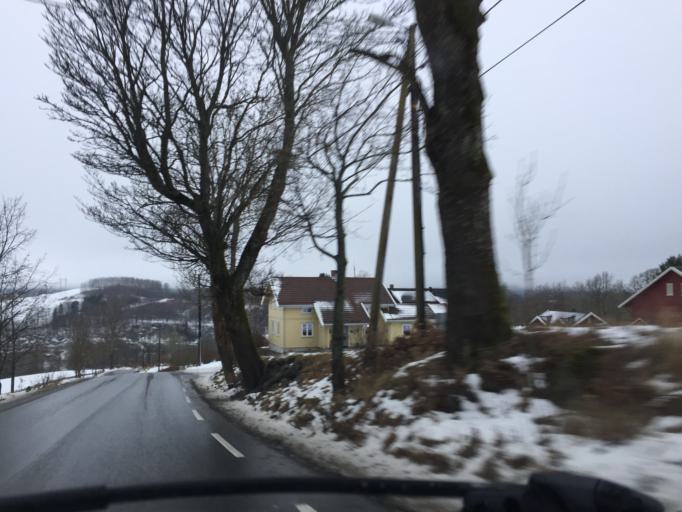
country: NO
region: Akershus
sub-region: As
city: As
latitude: 59.7022
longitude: 10.7492
